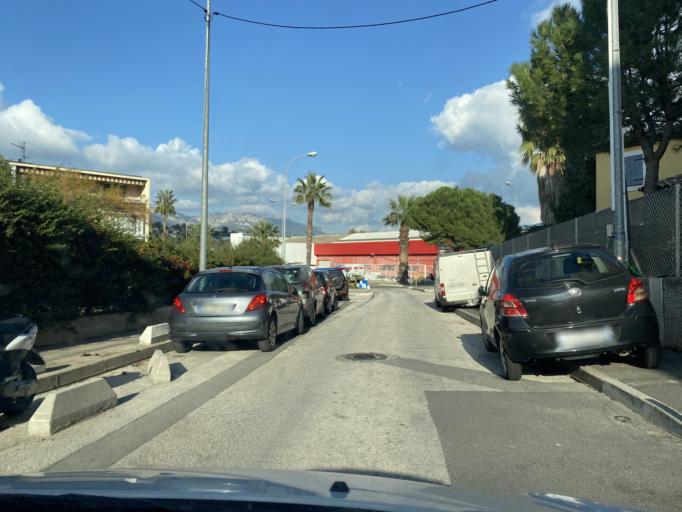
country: FR
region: Provence-Alpes-Cote d'Azur
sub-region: Departement du Var
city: La Seyne-sur-Mer
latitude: 43.1138
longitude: 5.8720
